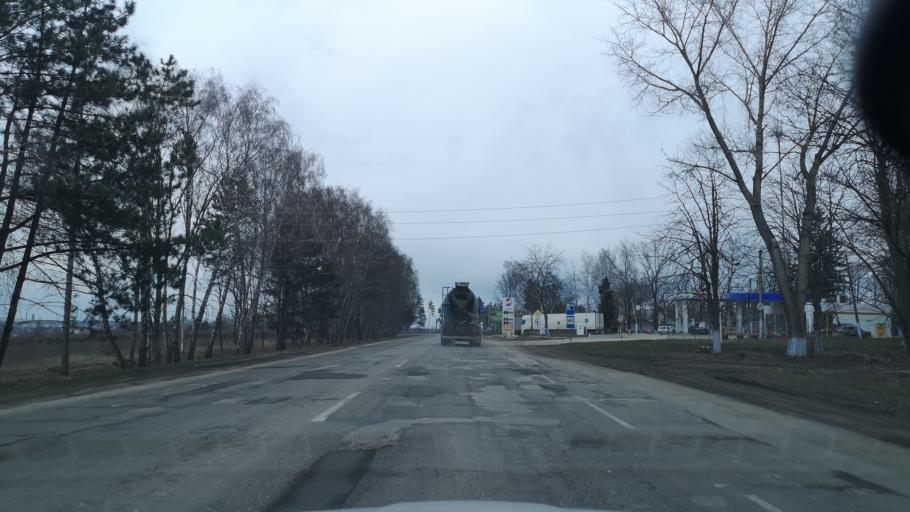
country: MD
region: Briceni
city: Briceni
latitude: 48.3499
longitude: 27.1025
